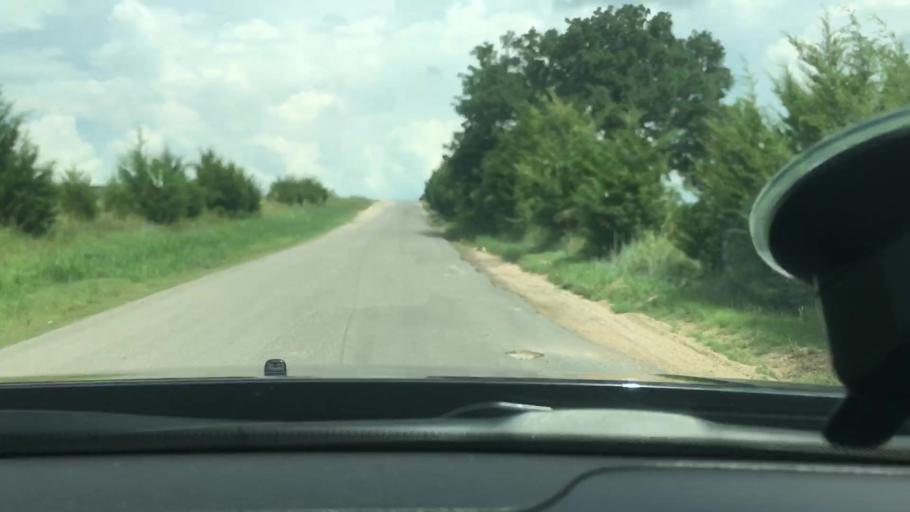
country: US
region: Oklahoma
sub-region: Carter County
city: Dickson
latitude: 34.1875
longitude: -96.8982
